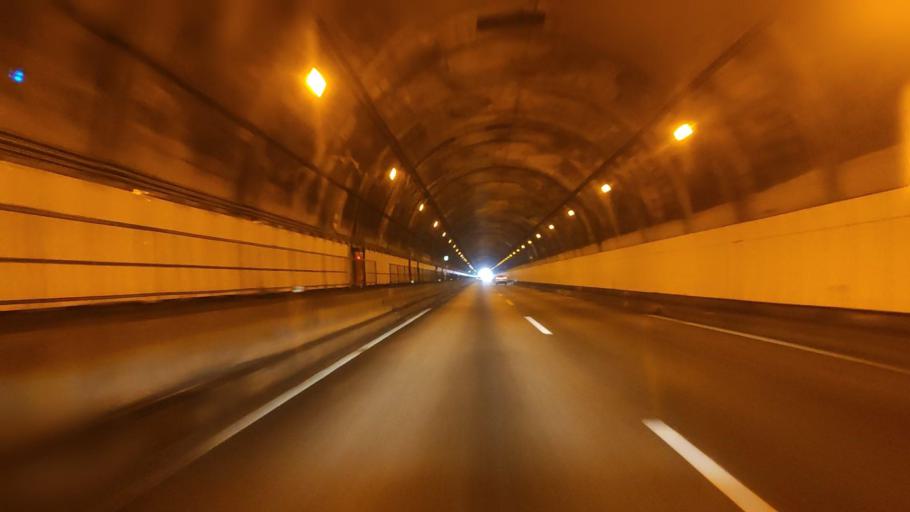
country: JP
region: Miyazaki
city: Miyakonojo
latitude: 31.8231
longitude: 131.2426
